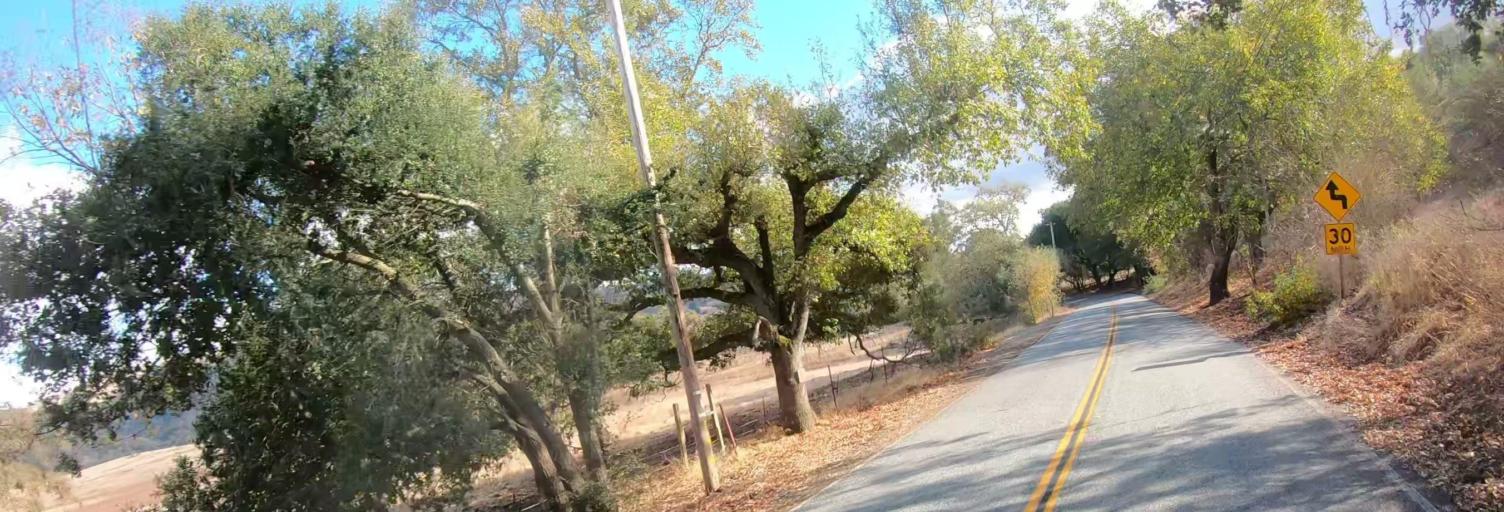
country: US
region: California
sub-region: Santa Clara County
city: East Foothills
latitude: 37.3474
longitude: -121.7274
